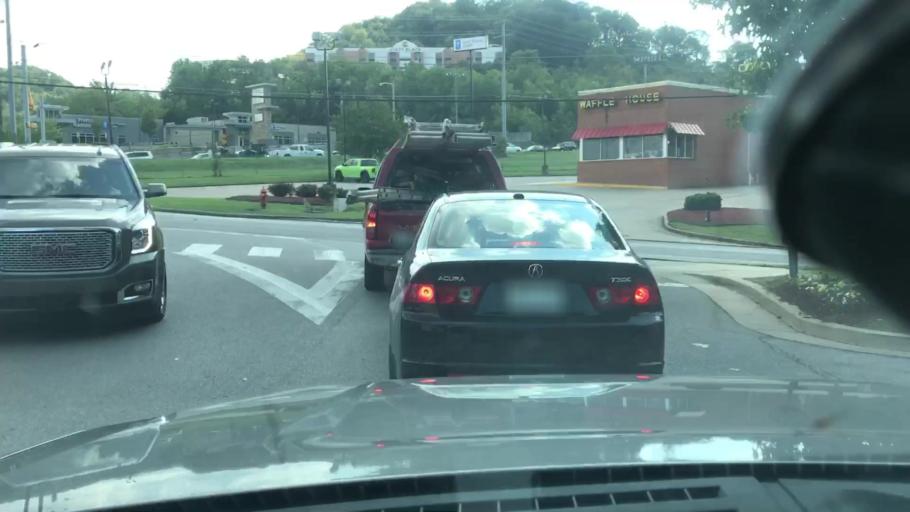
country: US
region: Tennessee
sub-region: Williamson County
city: Brentwood
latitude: 36.0416
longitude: -86.7799
